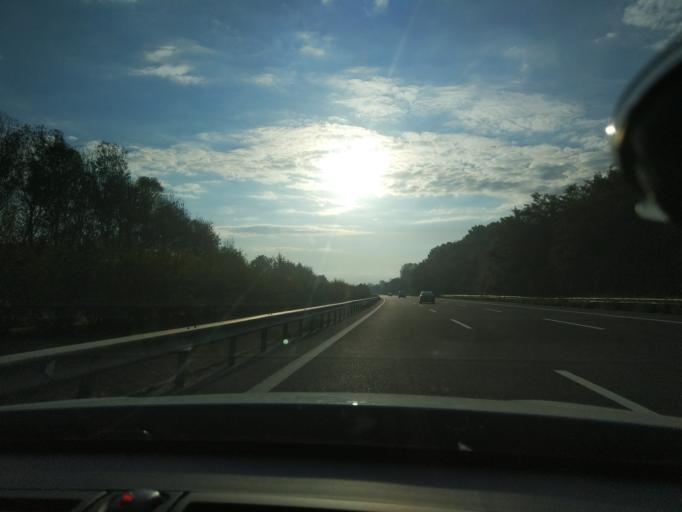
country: TR
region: Duzce
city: Duzce
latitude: 40.8067
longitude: 31.1508
